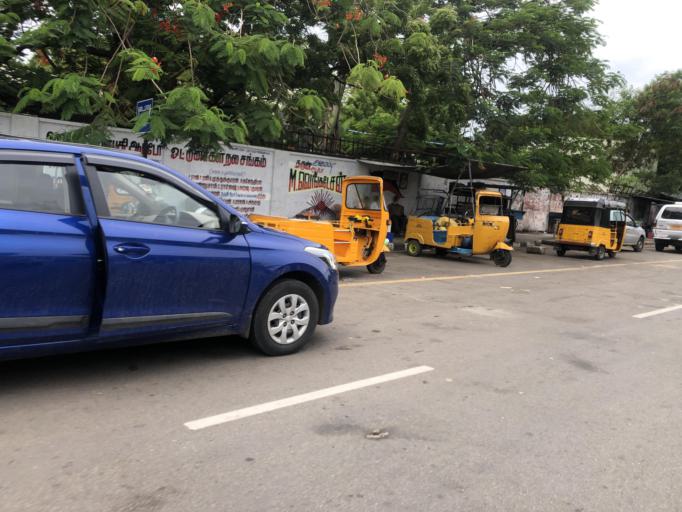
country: IN
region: Tamil Nadu
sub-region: Chennai
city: Chennai
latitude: 13.0762
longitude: 80.2763
